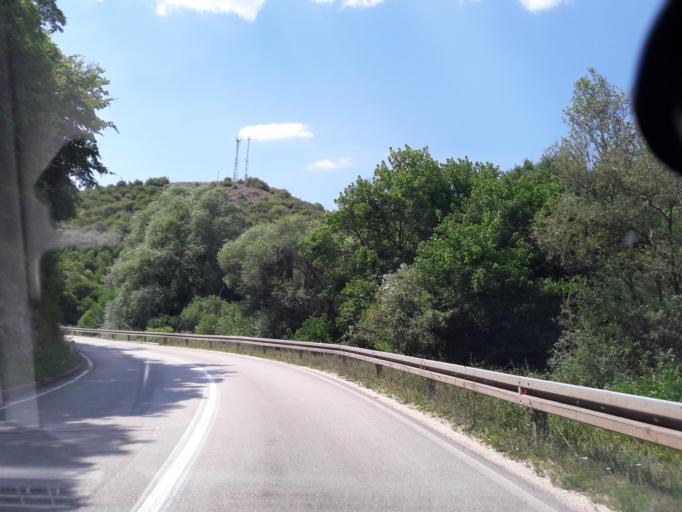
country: BA
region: Republika Srpska
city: Mrkonjic Grad
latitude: 44.4541
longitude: 17.1618
